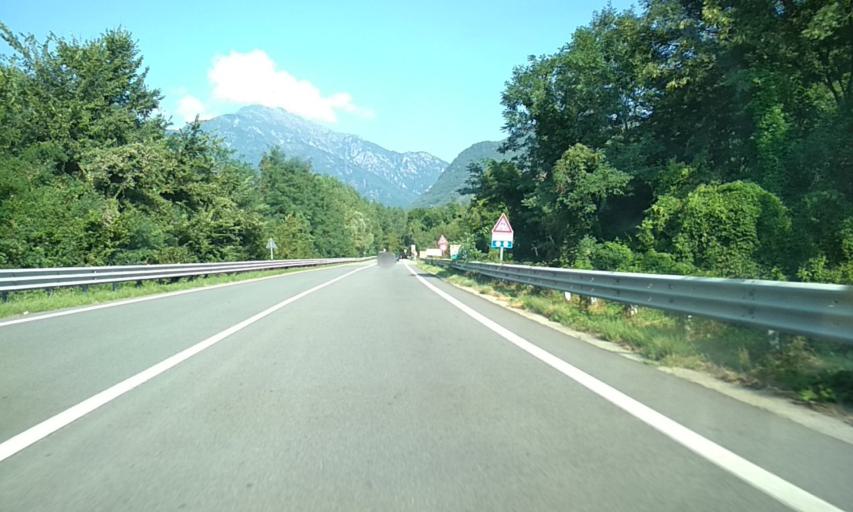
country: IT
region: Piedmont
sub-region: Provincia di Torino
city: San Colombano Belmonte
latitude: 45.4075
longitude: 7.6263
